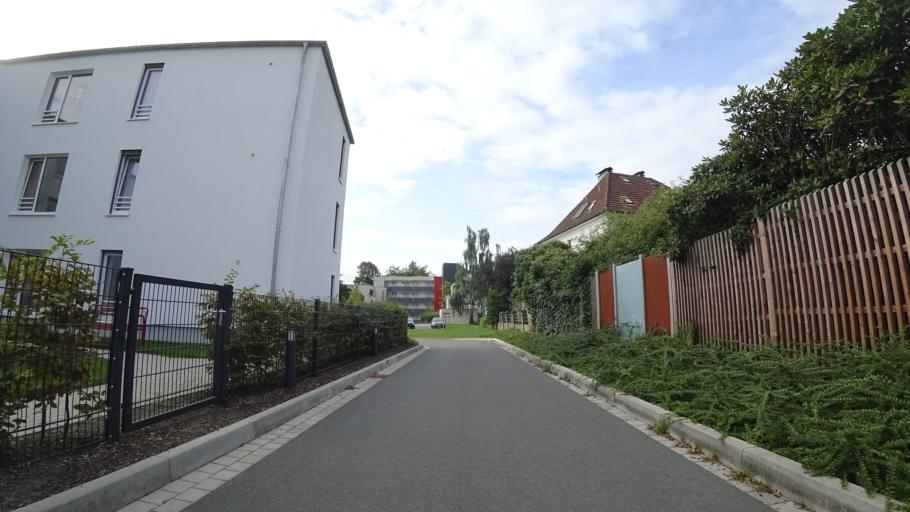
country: DE
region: North Rhine-Westphalia
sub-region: Regierungsbezirk Detmold
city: Bielefeld
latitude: 52.0442
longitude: 8.5425
